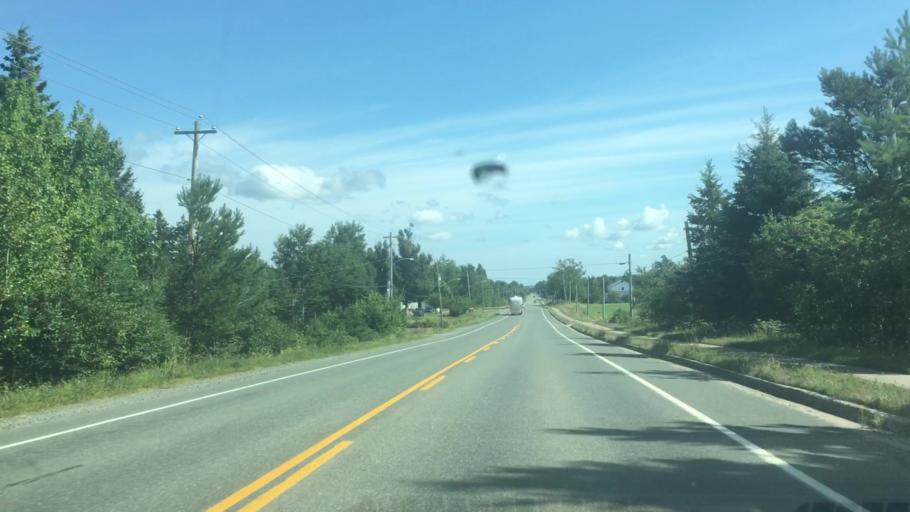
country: CA
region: Nova Scotia
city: Sydney
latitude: 46.0540
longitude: -60.3154
